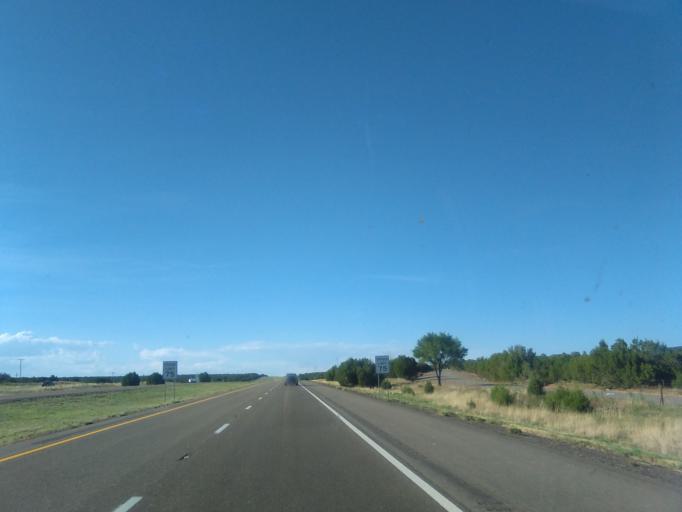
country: US
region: New Mexico
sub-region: San Miguel County
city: Las Vegas
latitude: 35.4660
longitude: -105.2762
